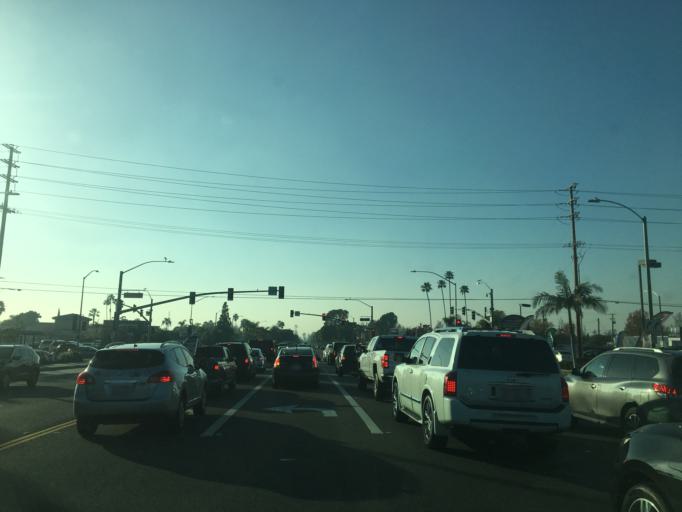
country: US
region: California
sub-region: Orange County
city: Orange
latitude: 33.7878
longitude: -117.8348
